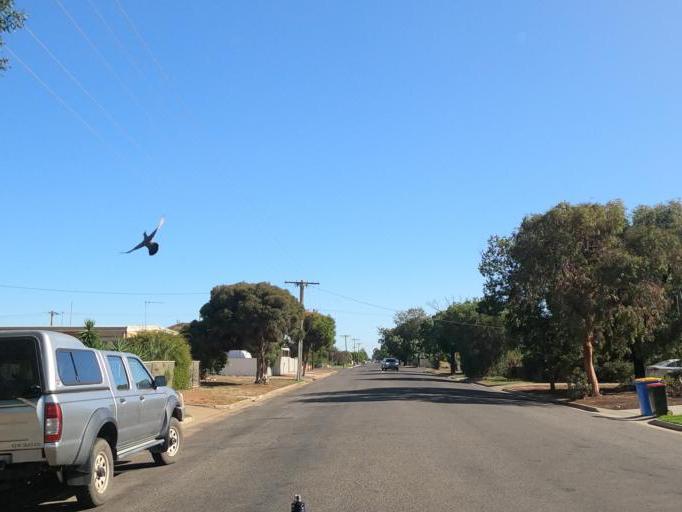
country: AU
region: Victoria
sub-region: Moira
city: Yarrawonga
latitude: -36.0159
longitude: 146.0073
